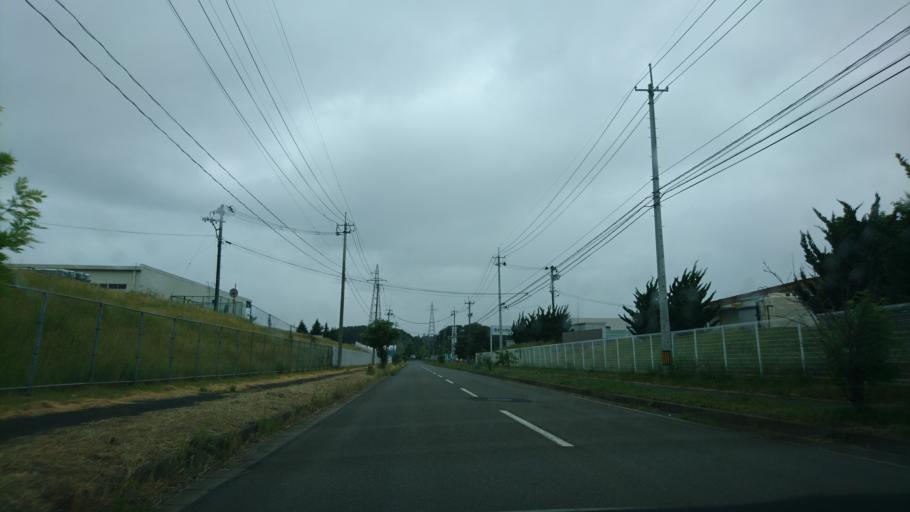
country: JP
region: Iwate
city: Ichinoseki
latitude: 38.9228
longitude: 141.1638
